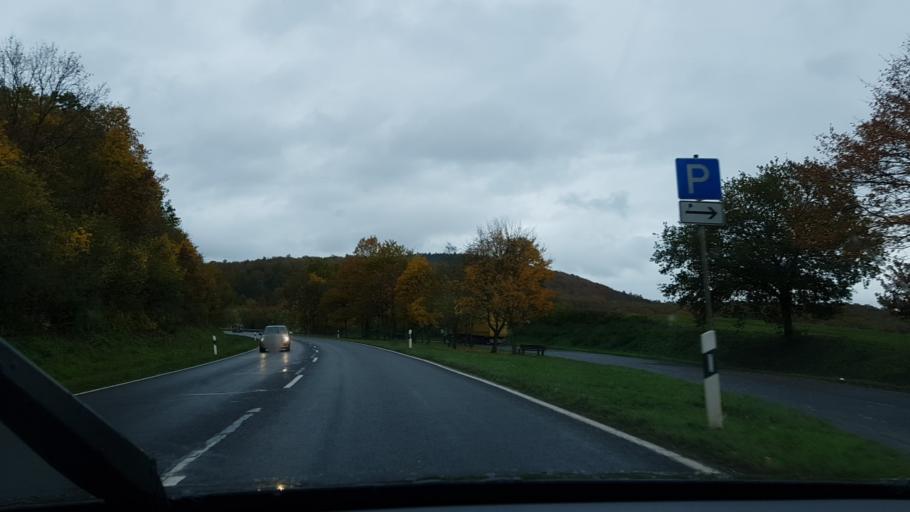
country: DE
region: Rheinland-Pfalz
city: Salmtal
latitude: 49.9377
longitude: 6.8506
